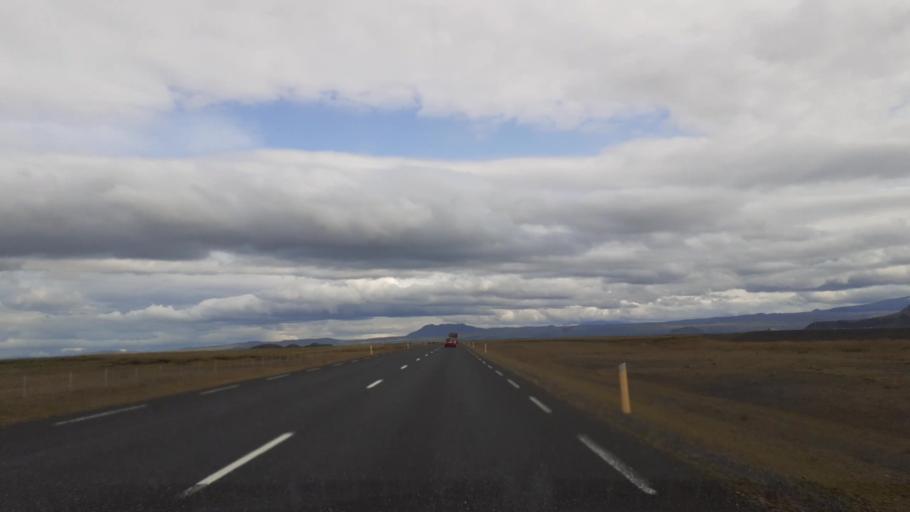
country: IS
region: South
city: Vestmannaeyjar
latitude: 63.5814
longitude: -20.0591
